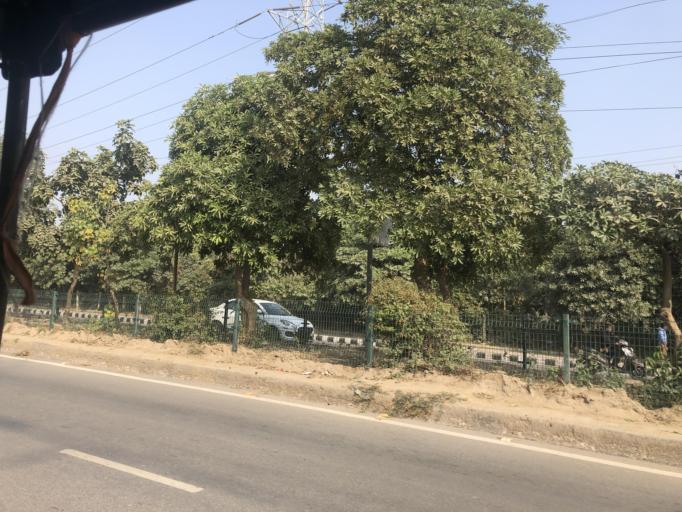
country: IN
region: Haryana
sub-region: Gurgaon
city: Gurgaon
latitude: 28.4428
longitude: 77.0844
